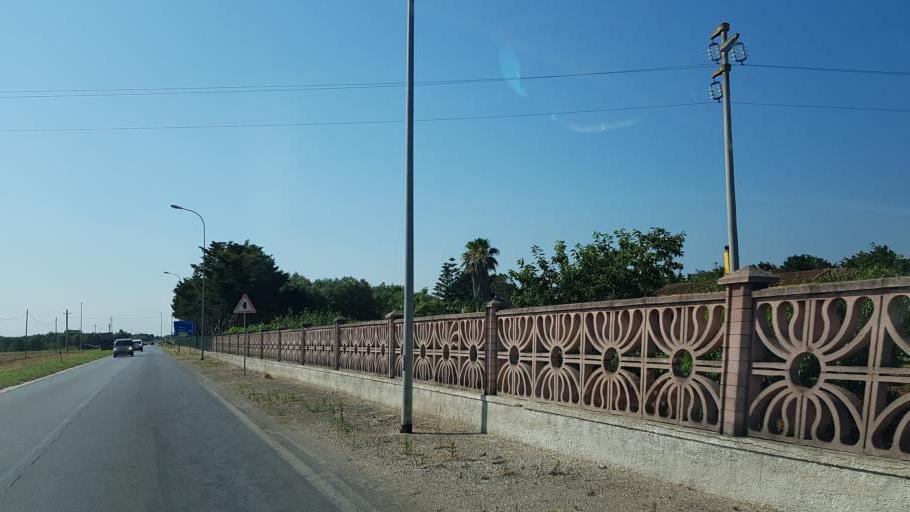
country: IT
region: Apulia
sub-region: Provincia di Brindisi
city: Mesagne
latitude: 40.5459
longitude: 17.8214
